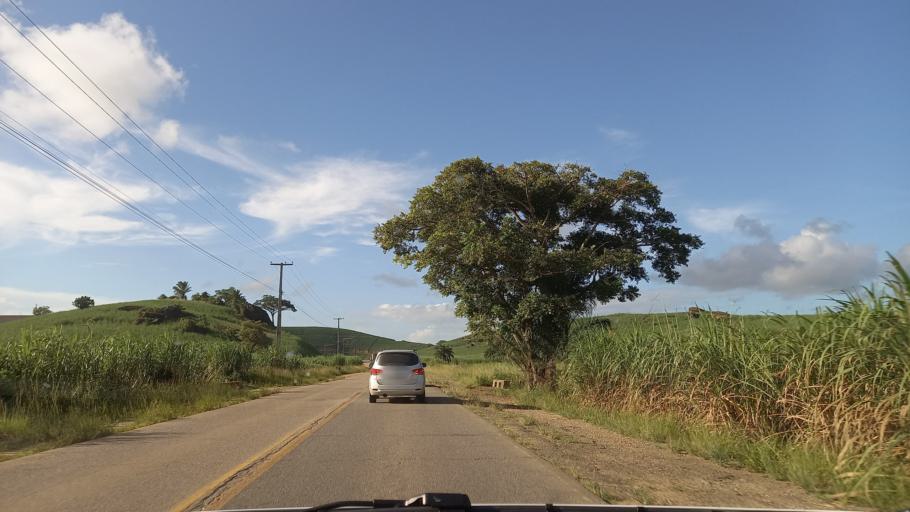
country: BR
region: Pernambuco
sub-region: Sirinhaem
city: Sirinhaem
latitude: -8.6079
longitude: -35.1175
